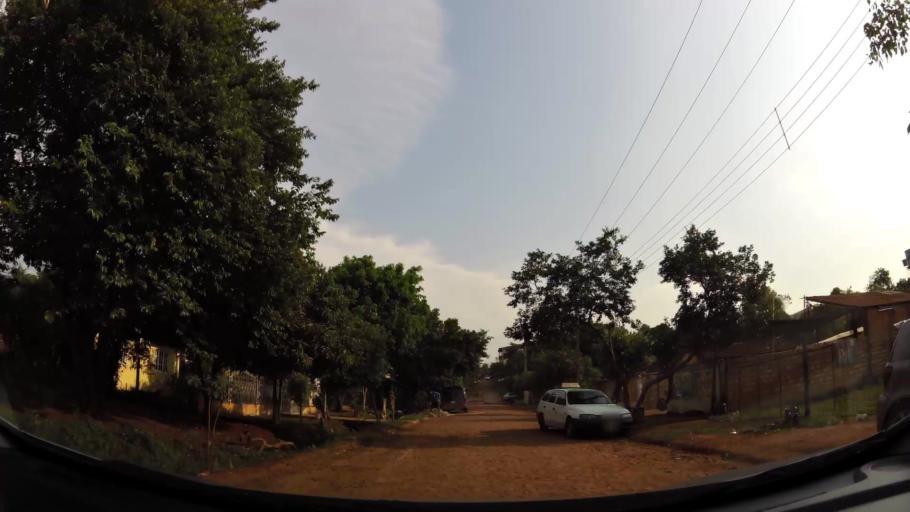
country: PY
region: Alto Parana
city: Ciudad del Este
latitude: -25.4812
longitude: -54.6716
